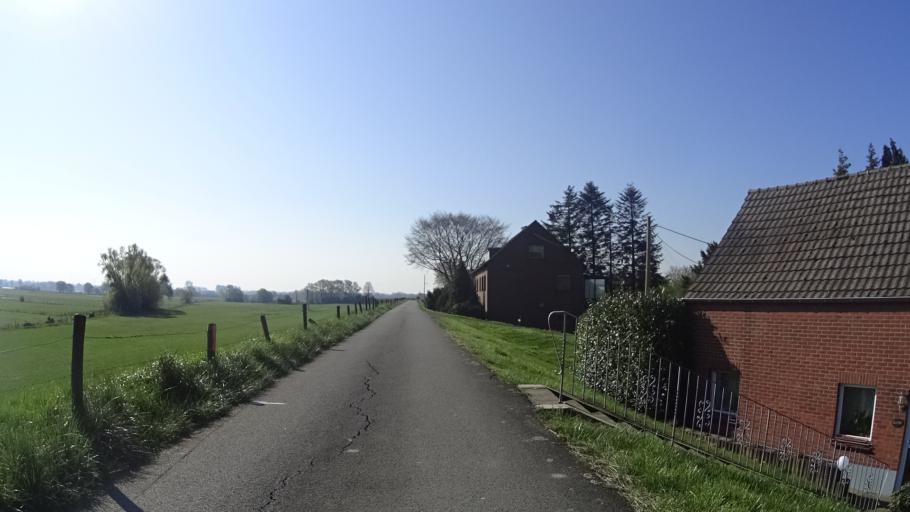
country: DE
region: North Rhine-Westphalia
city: Rheinberg
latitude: 51.5969
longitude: 6.5843
